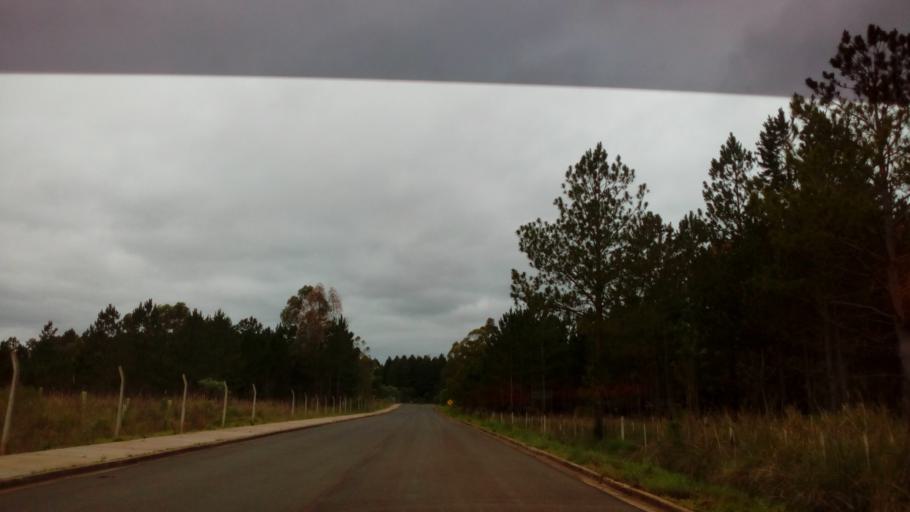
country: AR
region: Misiones
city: Garupa
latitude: -27.4577
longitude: -55.7950
